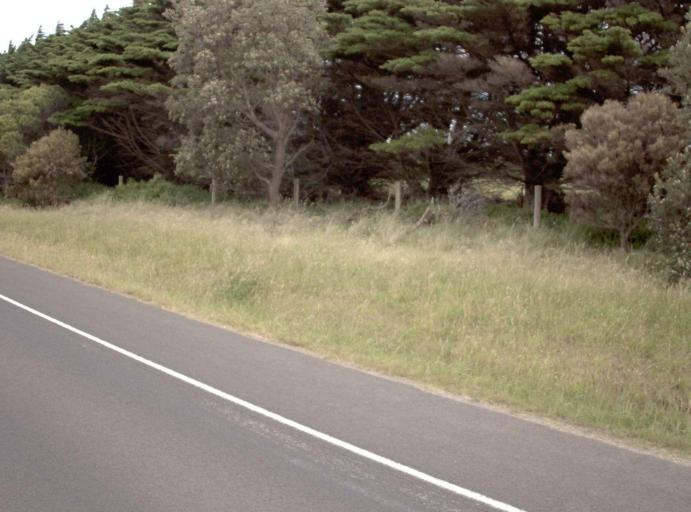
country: AU
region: Victoria
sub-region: Bass Coast
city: Phillip Island
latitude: -38.5160
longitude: 145.3142
